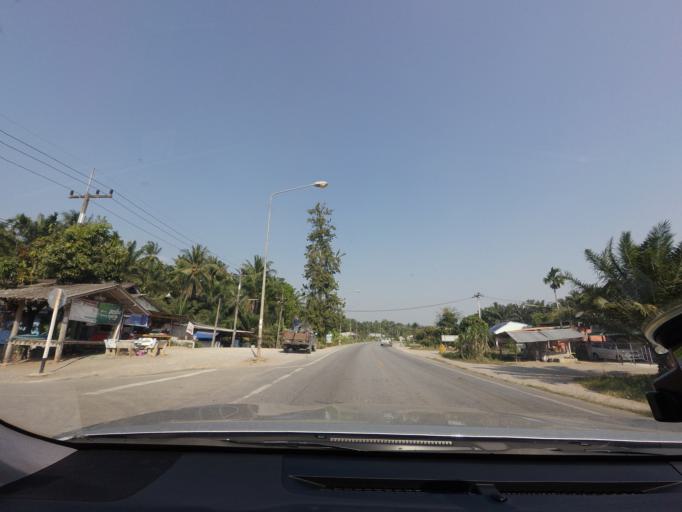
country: TH
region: Surat Thani
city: Chai Buri
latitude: 8.6026
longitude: 99.0132
